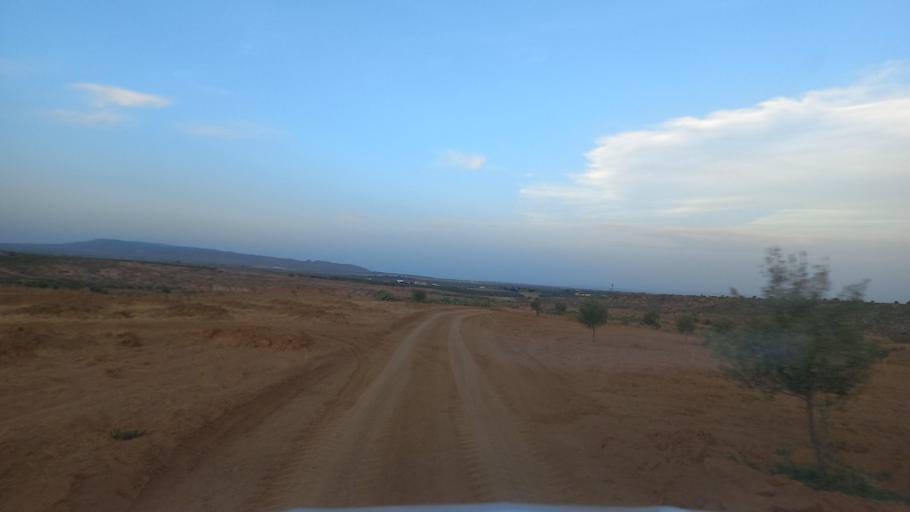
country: TN
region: Al Qasrayn
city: Kasserine
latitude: 35.1999
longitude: 9.0506
